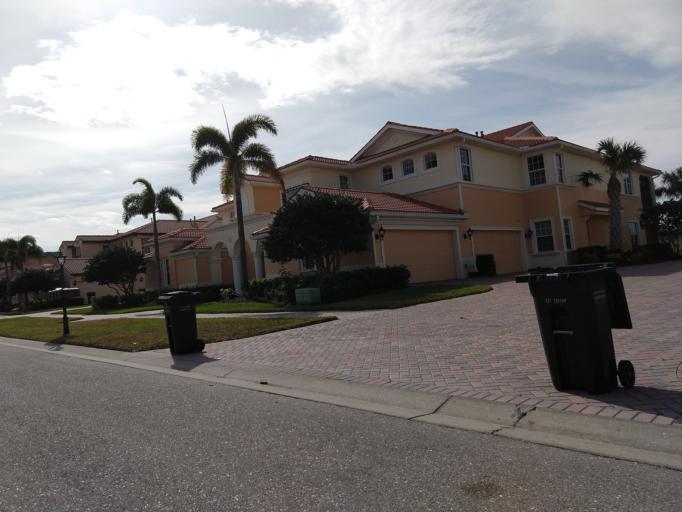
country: US
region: Florida
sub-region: Sarasota County
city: Nokomis
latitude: 27.1494
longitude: -82.3703
